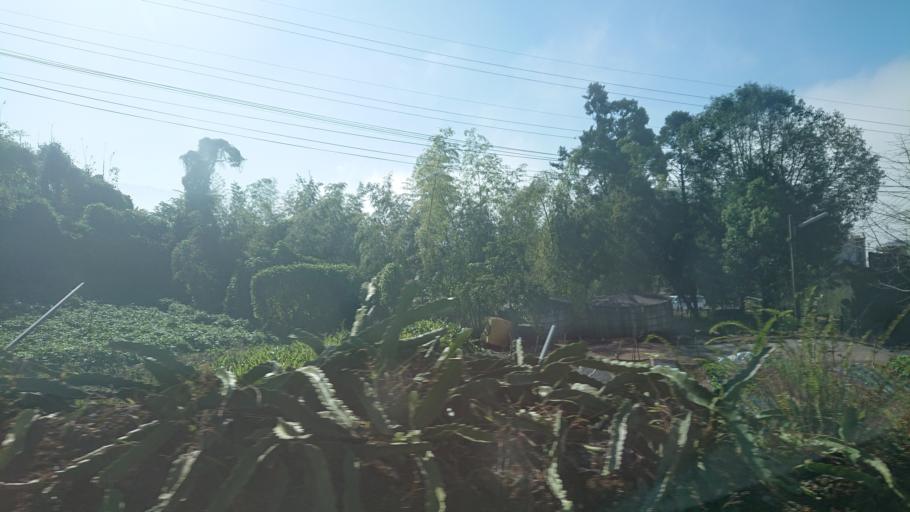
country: TW
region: Taiwan
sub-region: Chiayi
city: Jiayi Shi
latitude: 23.4781
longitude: 120.6978
